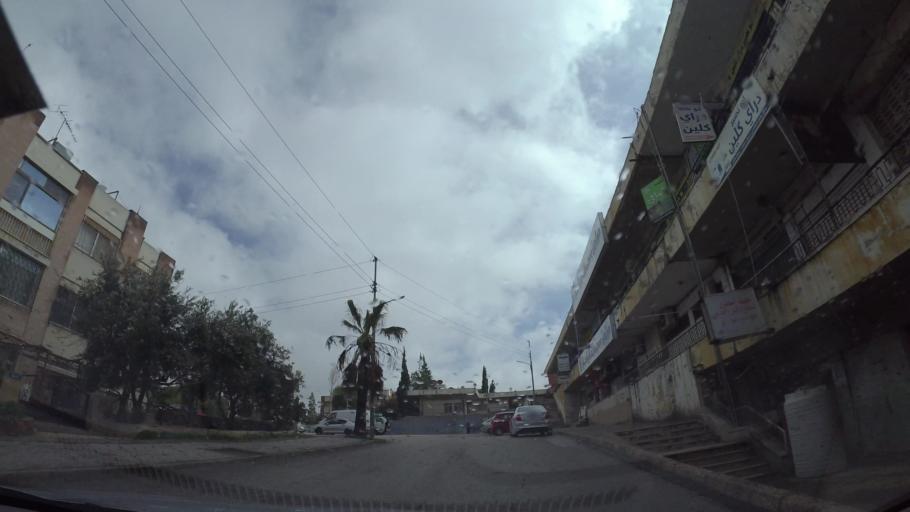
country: JO
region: Amman
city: Al Jubayhah
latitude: 32.0527
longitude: 35.8776
